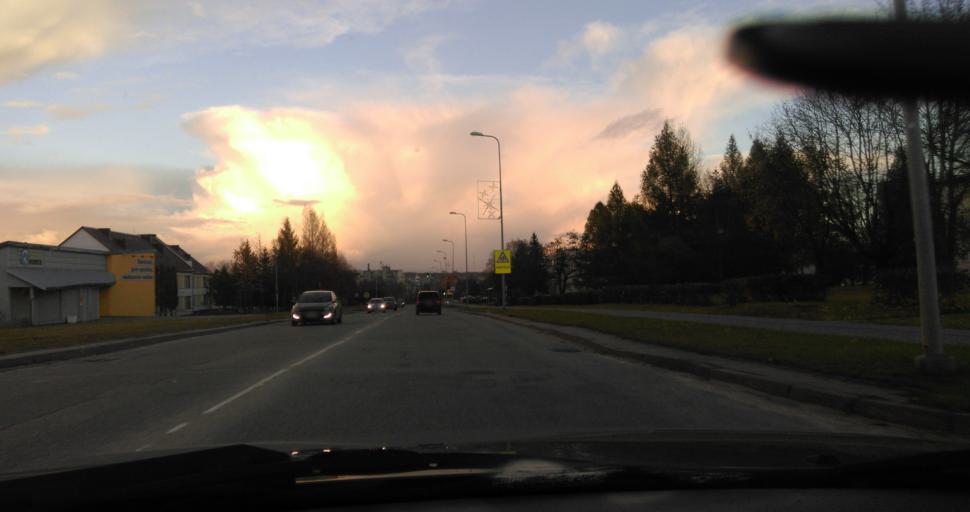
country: LT
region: Utenos apskritis
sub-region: Utena
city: Utena
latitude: 55.5104
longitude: 25.5883
